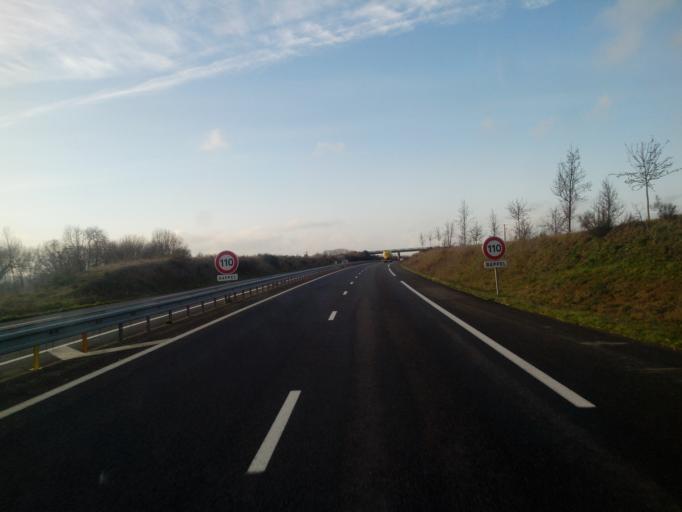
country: FR
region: Poitou-Charentes
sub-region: Departement des Deux-Sevres
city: Saint-Pierre-des-Echaubrognes
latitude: 46.9311
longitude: -0.7336
